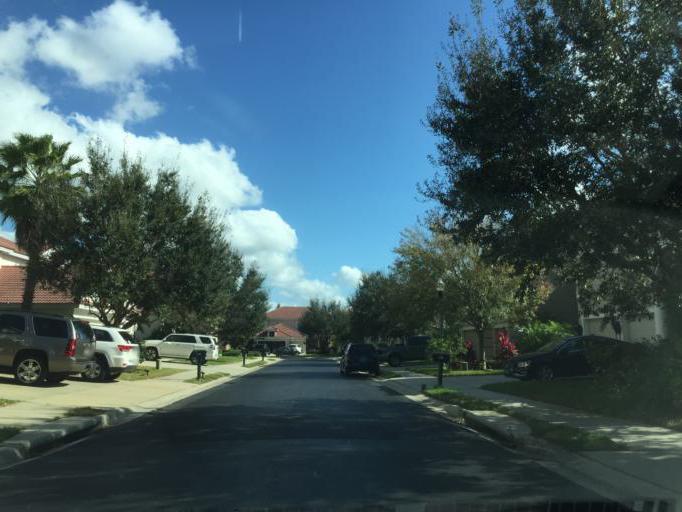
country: US
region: Florida
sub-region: Pinellas County
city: Saint George
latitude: 28.0428
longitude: -82.7429
